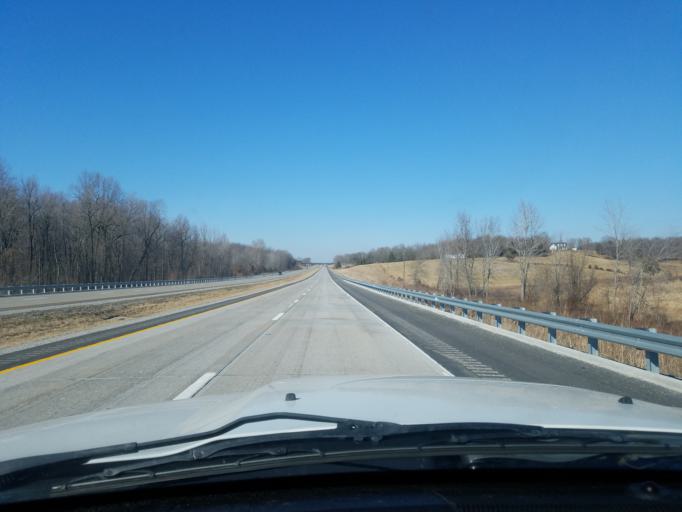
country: US
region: Kentucky
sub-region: Ohio County
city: Beaver Dam
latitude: 37.4023
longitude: -86.8219
